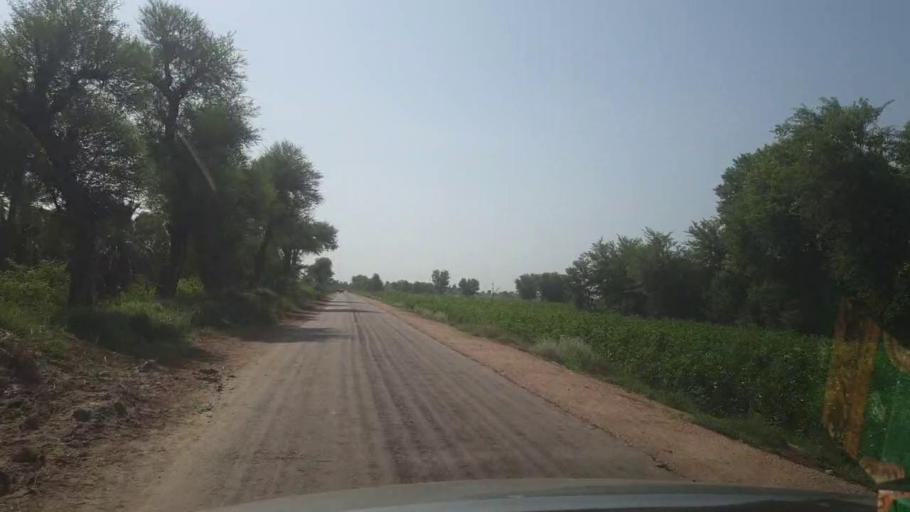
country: PK
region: Sindh
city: Rohri
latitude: 27.4732
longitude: 69.0308
